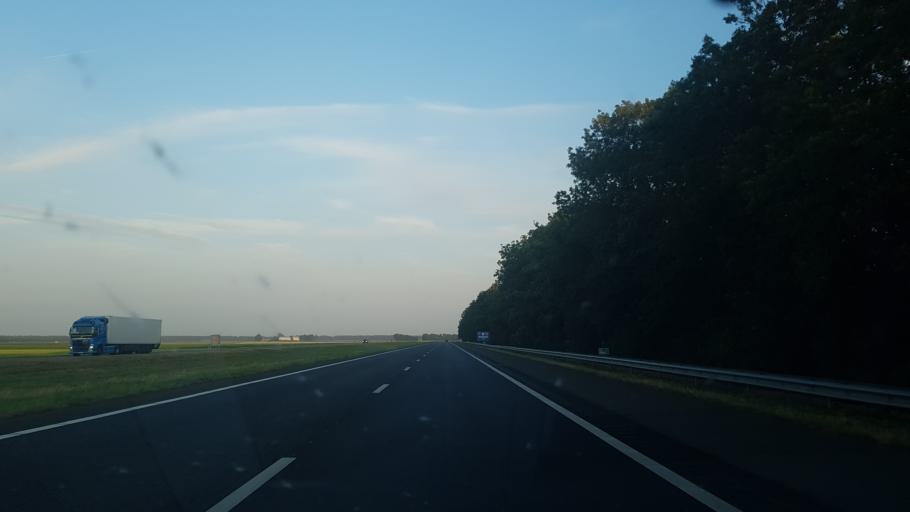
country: NL
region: Friesland
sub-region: Gemeente Lemsterland
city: Lemmer
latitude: 52.8282
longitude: 5.7348
